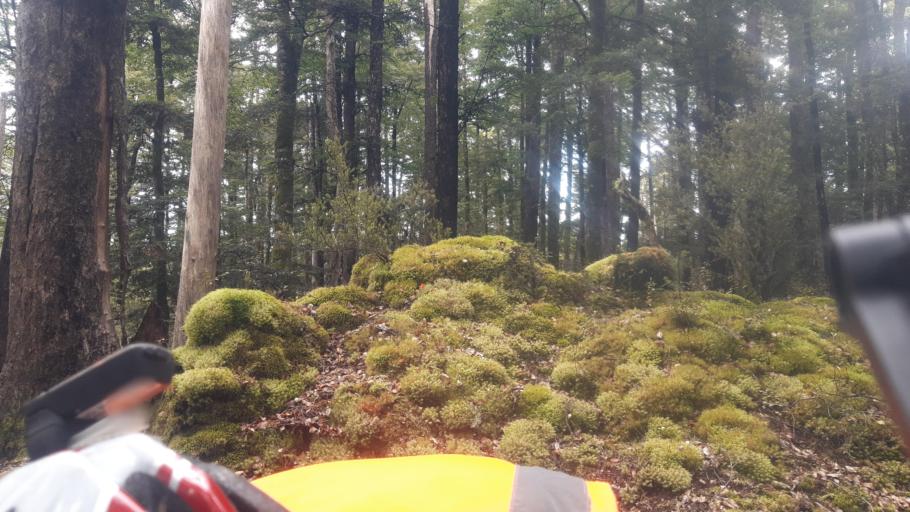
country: NZ
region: Tasman
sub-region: Tasman District
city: Wakefield
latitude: -41.7734
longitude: 172.8069
